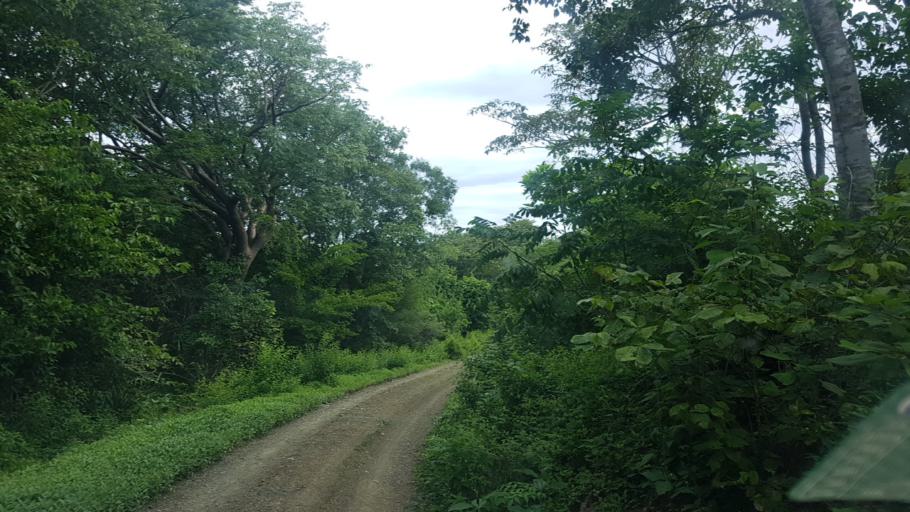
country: NI
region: Nueva Segovia
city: Ciudad Antigua
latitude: 13.5975
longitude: -86.3677
